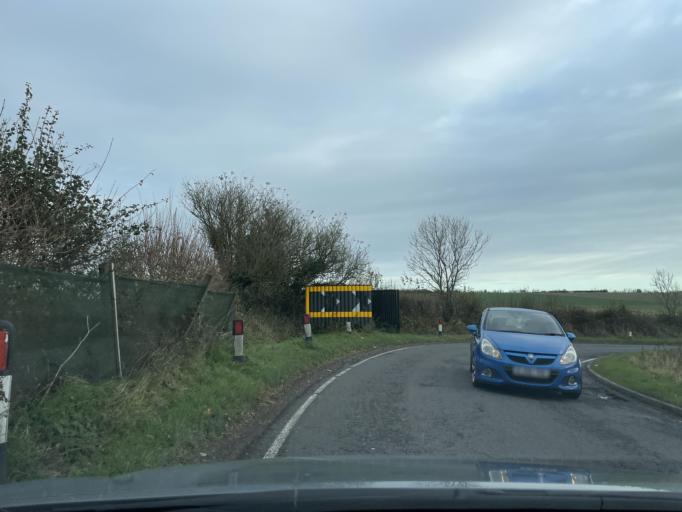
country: GB
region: England
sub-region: Borough of Swindon
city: Wroughton
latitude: 51.5075
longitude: -1.8236
